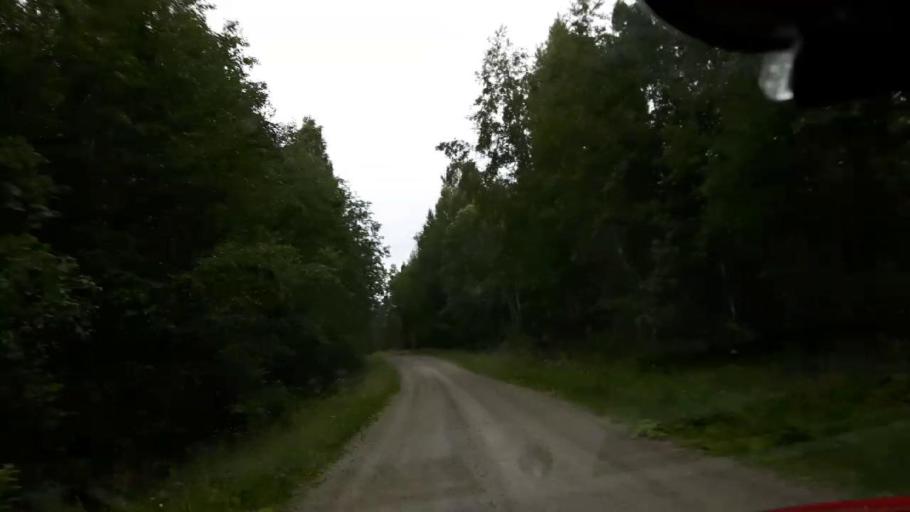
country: SE
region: Vaesternorrland
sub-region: Ange Kommun
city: Ange
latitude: 62.7864
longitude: 15.7729
